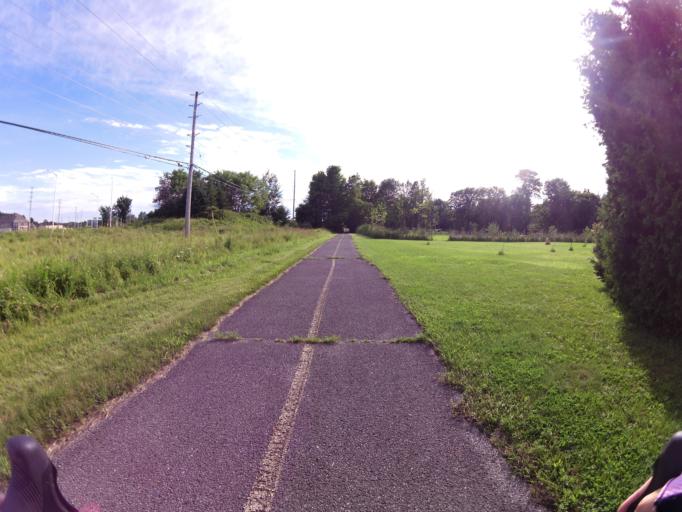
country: CA
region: Ontario
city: Bells Corners
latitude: 45.2765
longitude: -75.7858
